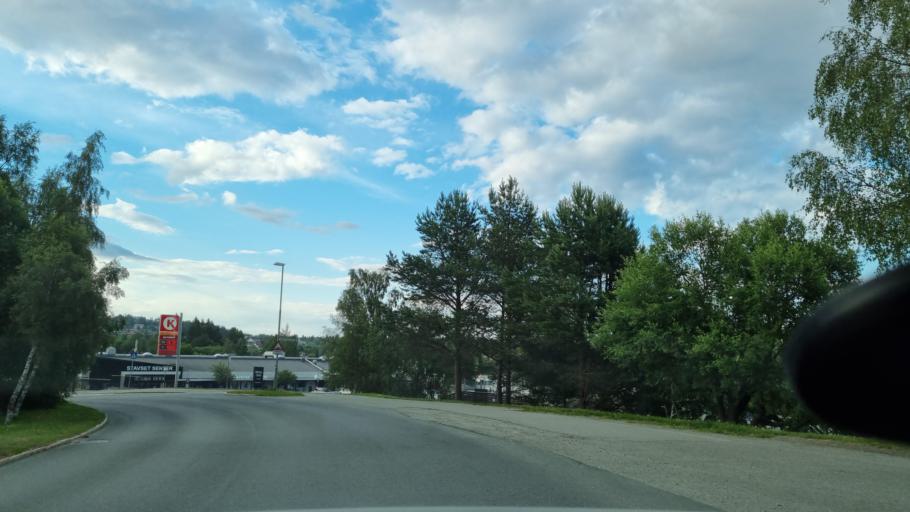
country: NO
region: Sor-Trondelag
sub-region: Trondheim
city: Trondheim
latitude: 63.3862
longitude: 10.3305
